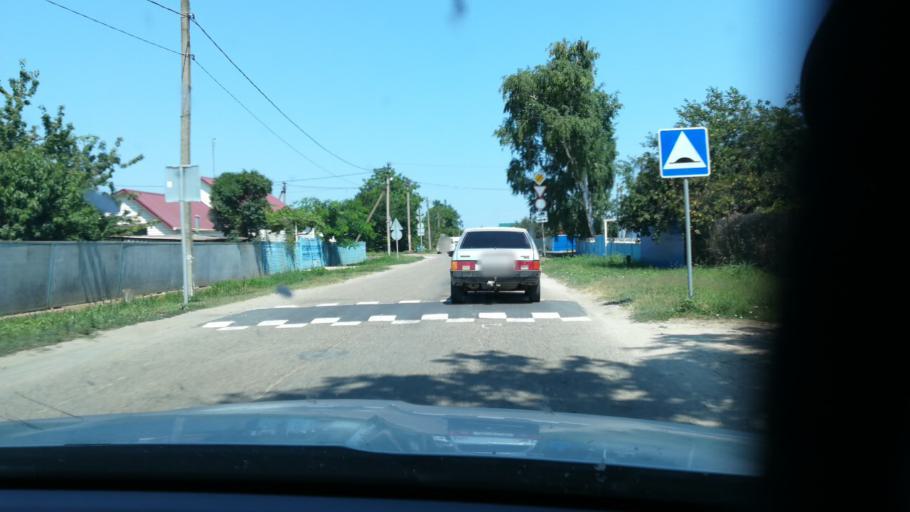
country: RU
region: Krasnodarskiy
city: Starotitarovskaya
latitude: 45.2055
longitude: 37.1470
